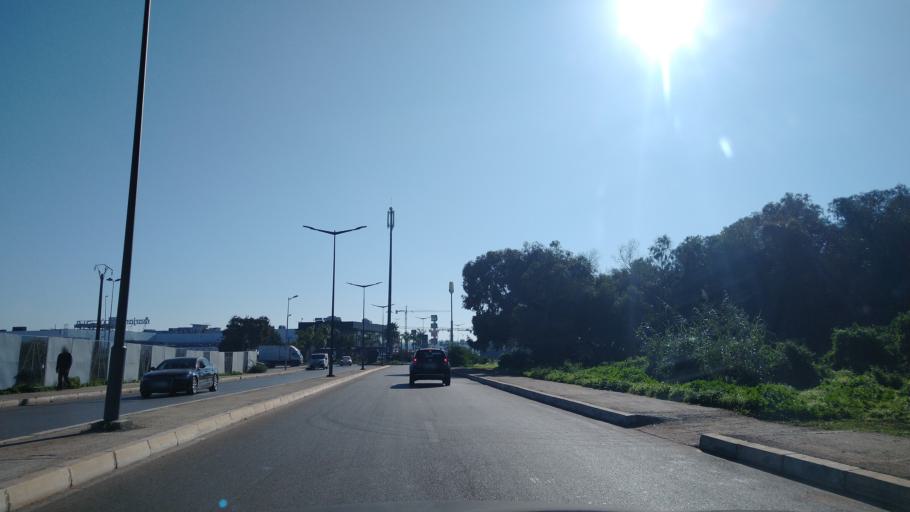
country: MA
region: Rabat-Sale-Zemmour-Zaer
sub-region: Skhirate-Temara
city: Temara
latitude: 33.9542
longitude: -6.8564
